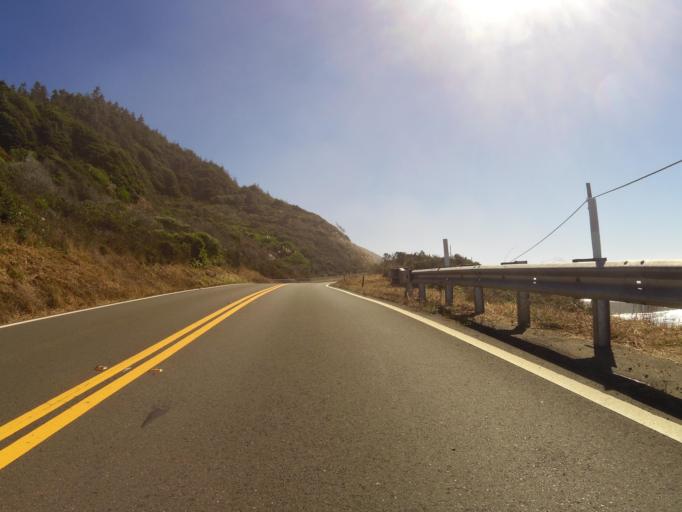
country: US
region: California
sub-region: Mendocino County
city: Fort Bragg
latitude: 39.6123
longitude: -123.7822
